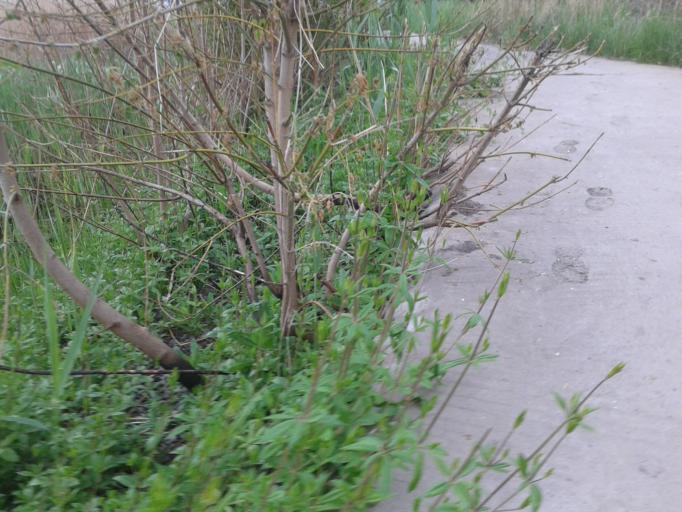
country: RU
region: Volgograd
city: Krasnoslobodsk
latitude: 48.5196
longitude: 44.5107
